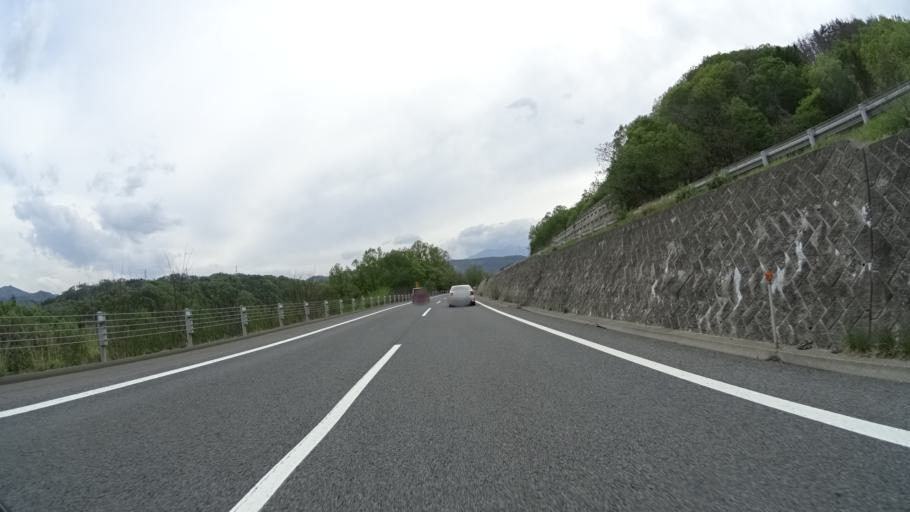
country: JP
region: Nagano
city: Toyoshina
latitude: 36.3571
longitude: 137.9842
